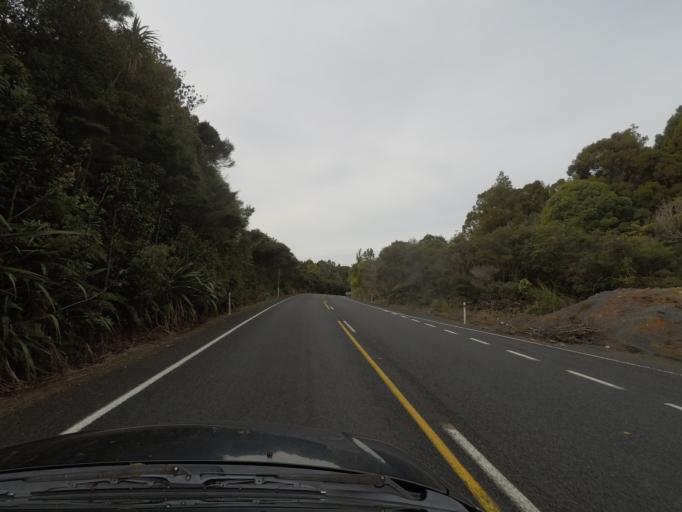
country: NZ
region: Auckland
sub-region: Auckland
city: Titirangi
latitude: -36.9435
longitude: 174.5329
